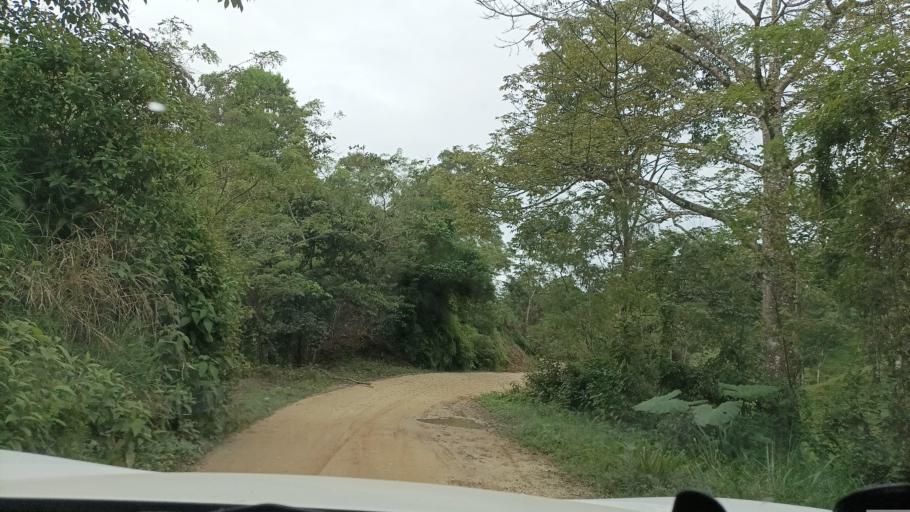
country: MX
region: Veracruz
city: Hidalgotitlan
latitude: 17.5755
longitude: -94.4228
